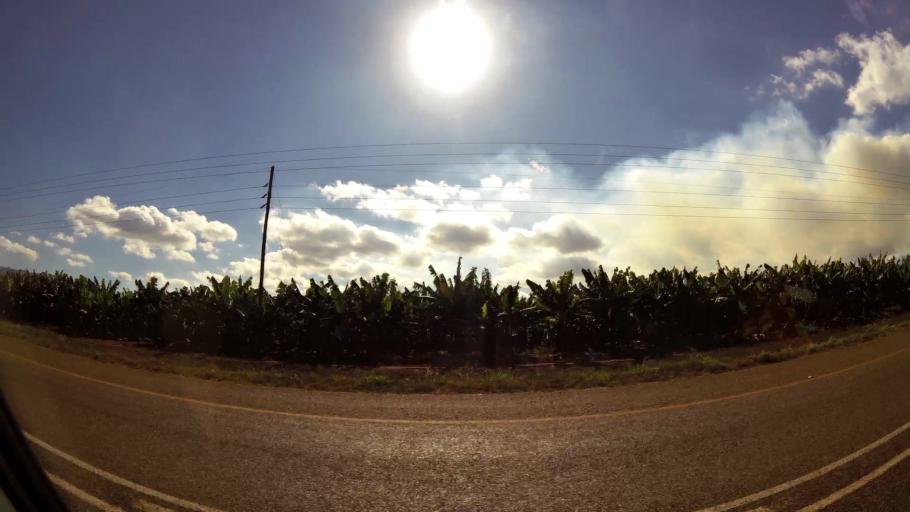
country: ZA
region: Limpopo
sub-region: Mopani District Municipality
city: Tzaneen
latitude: -23.8035
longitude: 30.1155
